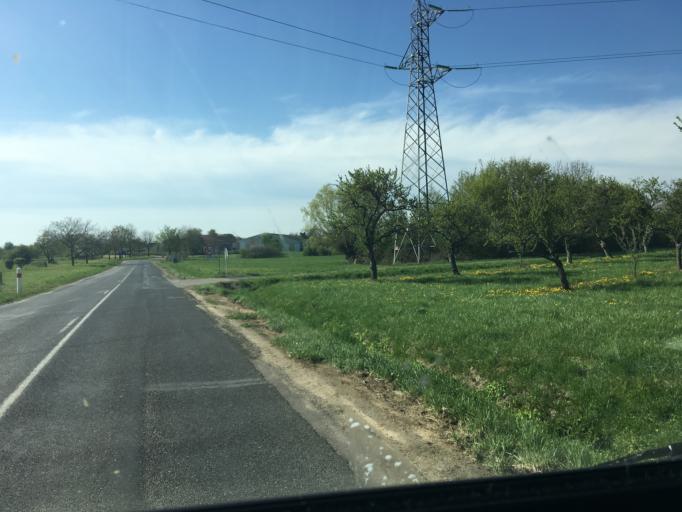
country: FR
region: Lorraine
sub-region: Departement de la Meuse
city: Vigneulles-les-Hattonchatel
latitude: 48.9359
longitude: 5.6999
